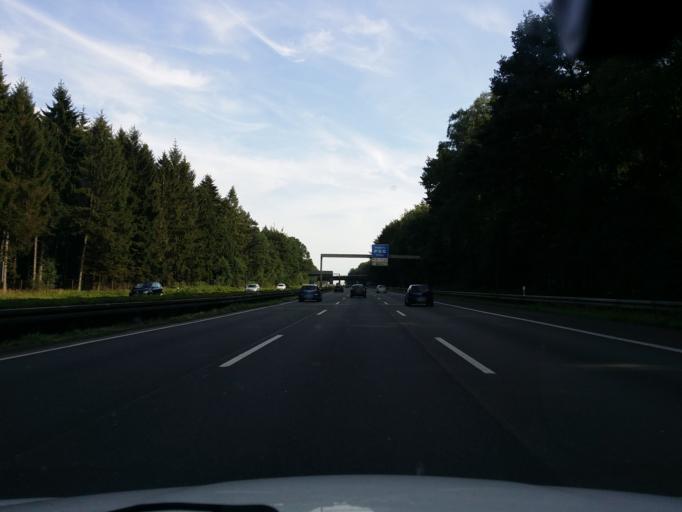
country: DE
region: North Rhine-Westphalia
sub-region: Regierungsbezirk Koln
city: Siegburg
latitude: 50.8183
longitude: 7.2092
